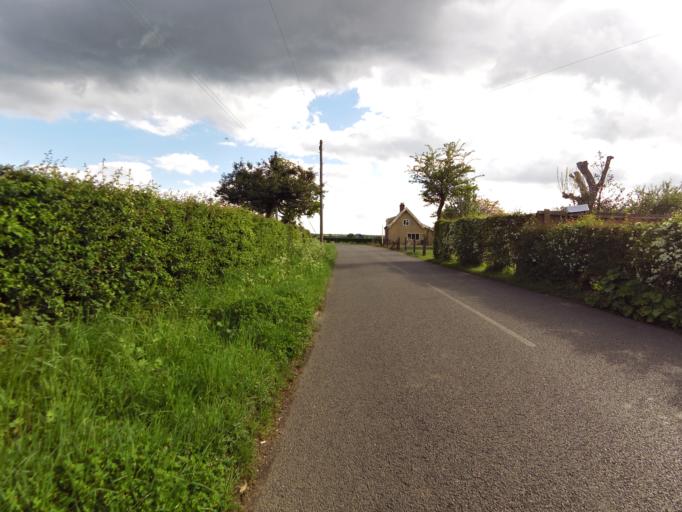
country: GB
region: England
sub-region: Suffolk
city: Elmswell
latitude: 52.2003
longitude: 0.9470
